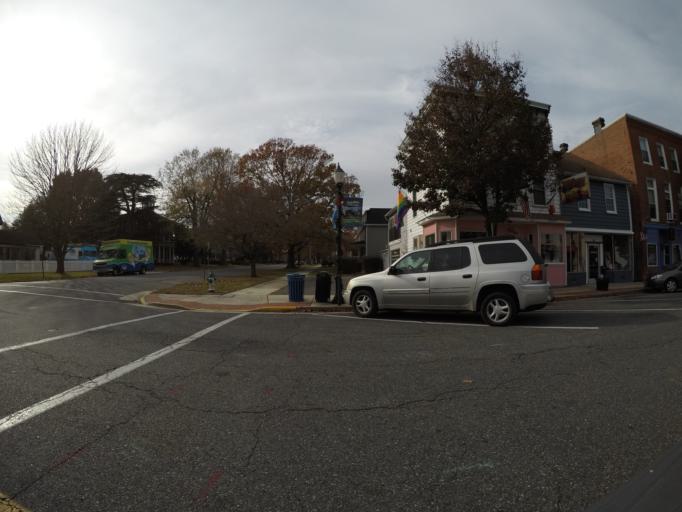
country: US
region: Maryland
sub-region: Harford County
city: Havre de Grace
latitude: 39.5478
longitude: -76.0898
